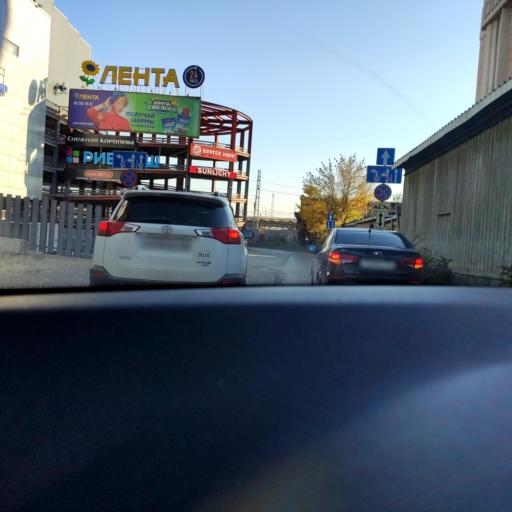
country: RU
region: Samara
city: Samara
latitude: 53.1867
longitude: 50.1247
